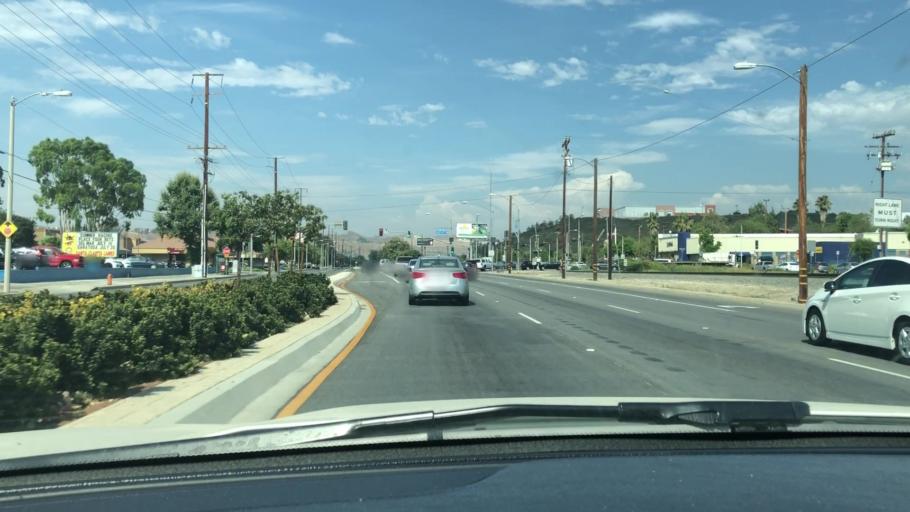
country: US
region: California
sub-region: Los Angeles County
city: Santa Clarita
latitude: 34.4157
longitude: -118.5143
